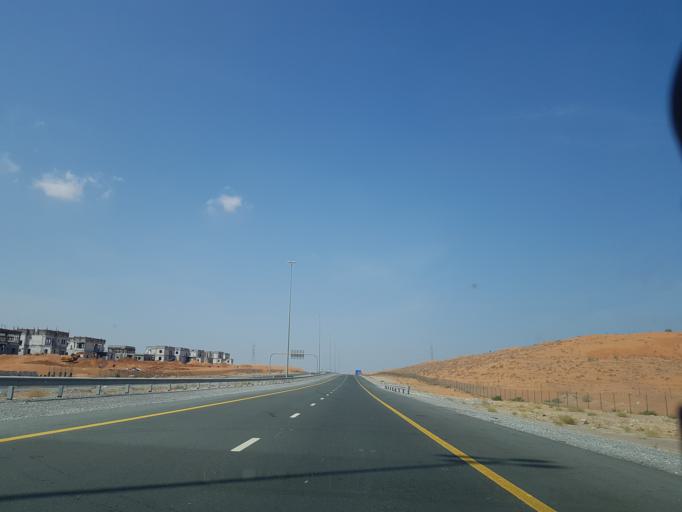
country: AE
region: Ra's al Khaymah
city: Ras al-Khaimah
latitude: 25.6676
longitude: 55.8919
